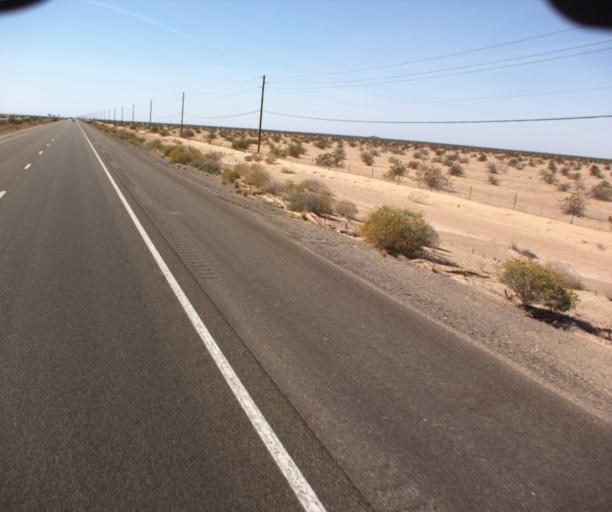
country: US
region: Arizona
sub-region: Yuma County
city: Somerton
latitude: 32.4948
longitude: -114.6640
